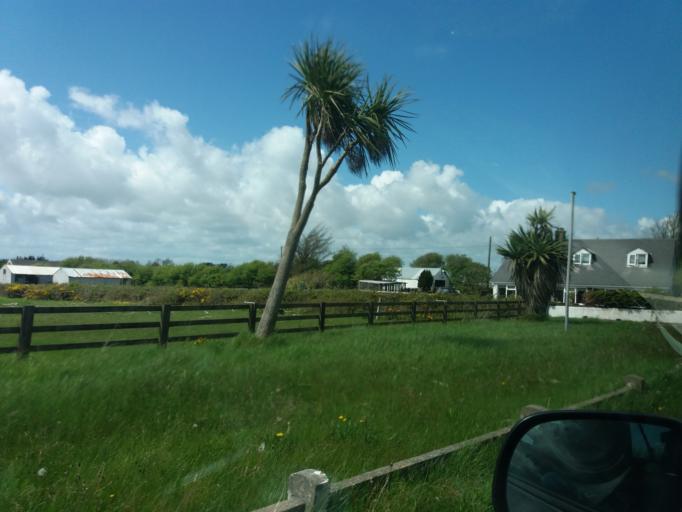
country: IE
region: Munster
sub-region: Waterford
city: Dunmore East
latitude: 52.2098
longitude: -6.8977
